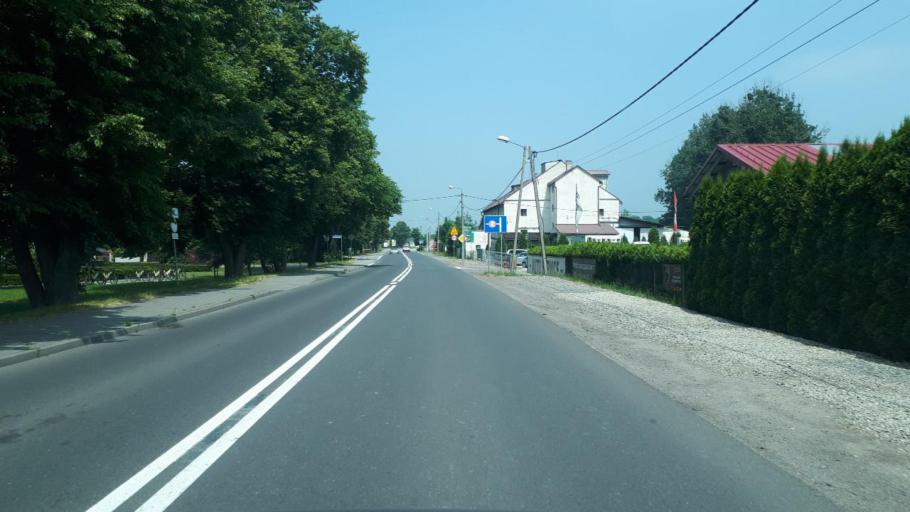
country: PL
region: Silesian Voivodeship
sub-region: Powiat cieszynski
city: Ustron
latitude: 49.7433
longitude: 18.8042
